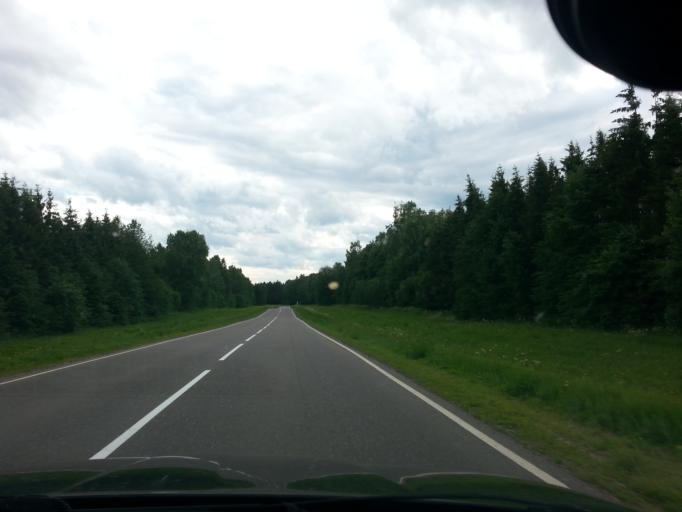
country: BY
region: Minsk
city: Svir
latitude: 54.8895
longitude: 26.3835
